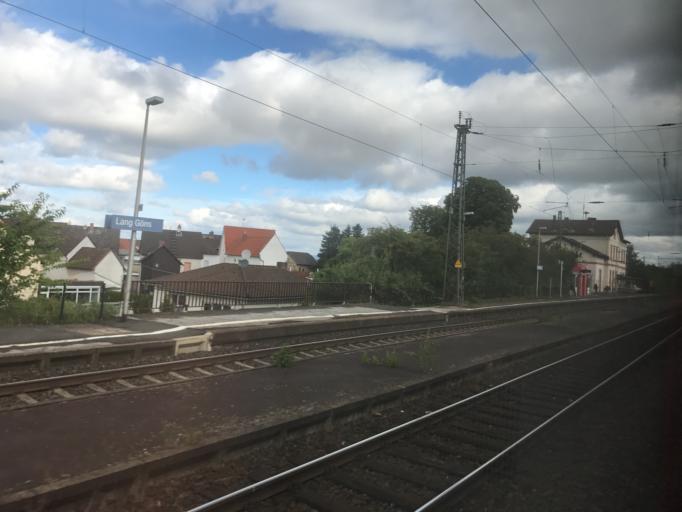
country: DE
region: Hesse
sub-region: Regierungsbezirk Giessen
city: Langgons
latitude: 50.4961
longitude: 8.6670
